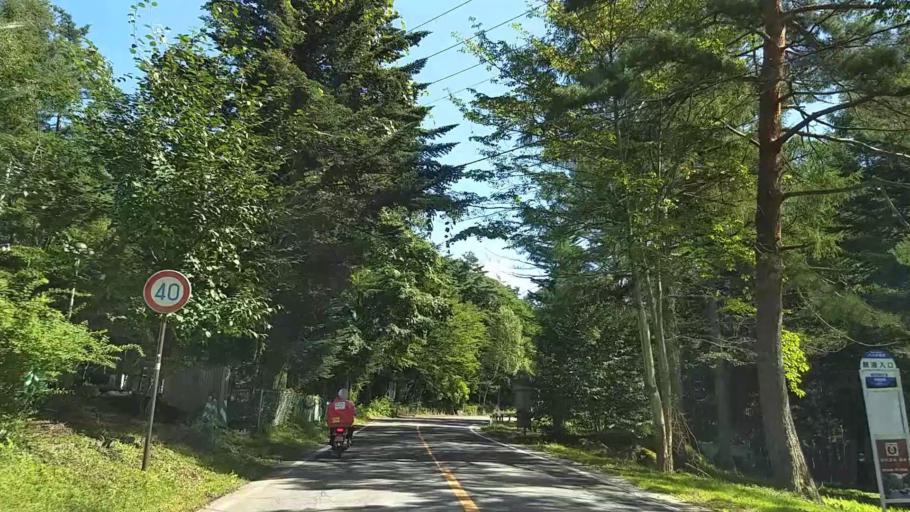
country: JP
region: Nagano
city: Chino
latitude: 36.0597
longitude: 138.2688
